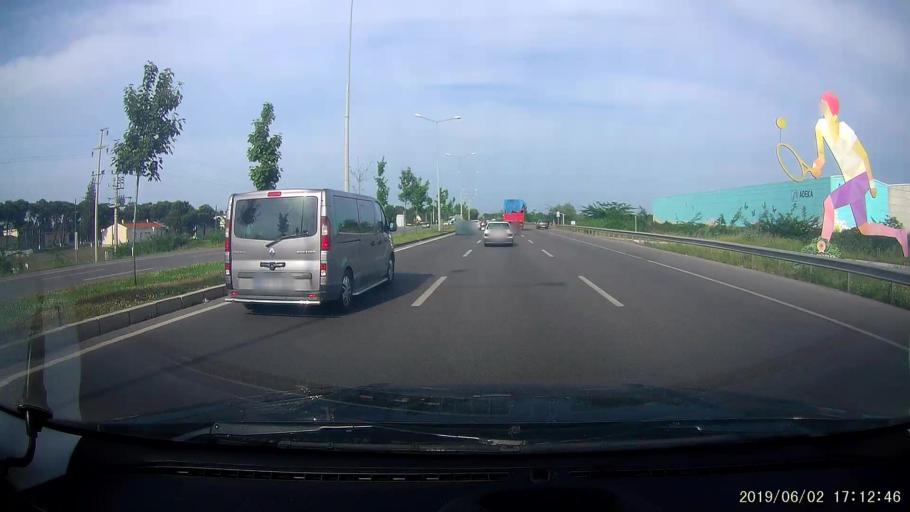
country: TR
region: Samsun
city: Tekkekoy
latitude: 41.2294
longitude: 36.4955
